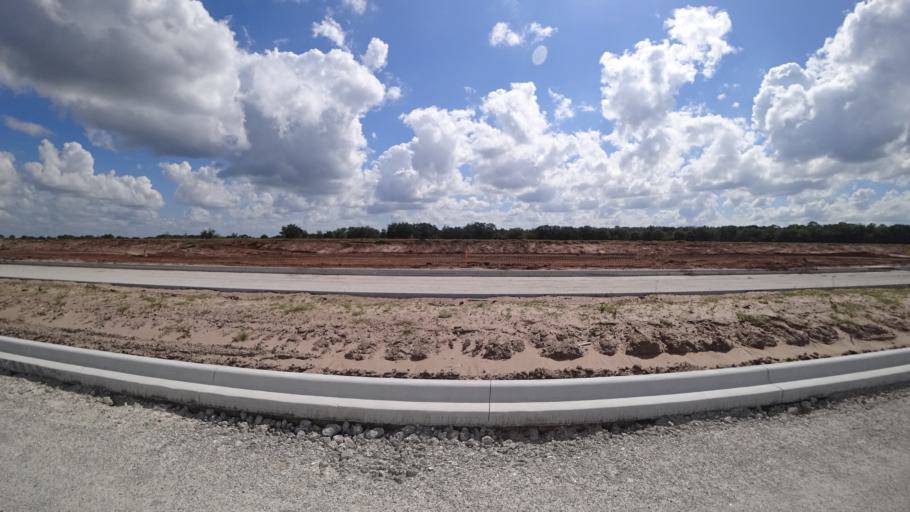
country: US
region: Florida
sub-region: Sarasota County
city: The Meadows
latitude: 27.4572
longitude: -82.3746
